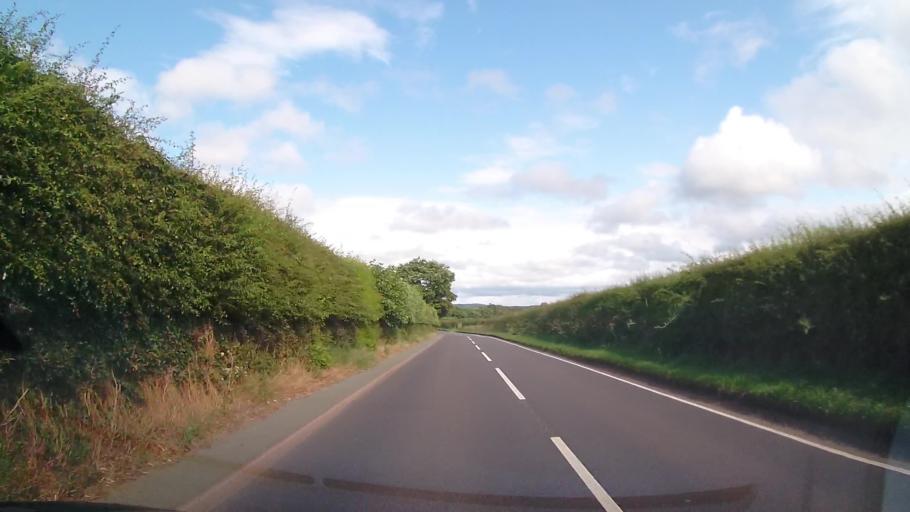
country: GB
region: England
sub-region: Shropshire
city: Great Ness
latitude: 52.7943
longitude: -2.8745
